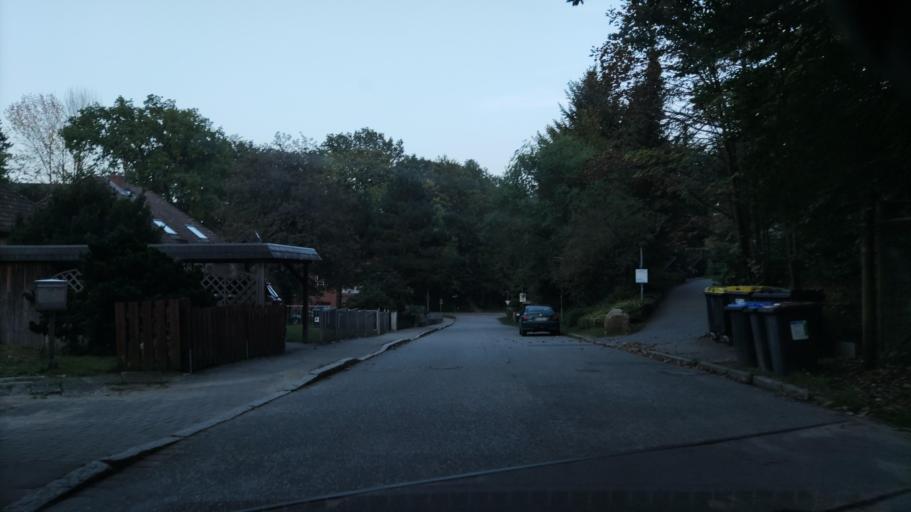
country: DE
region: Lower Saxony
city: Tespe
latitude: 53.4105
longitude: 10.4301
